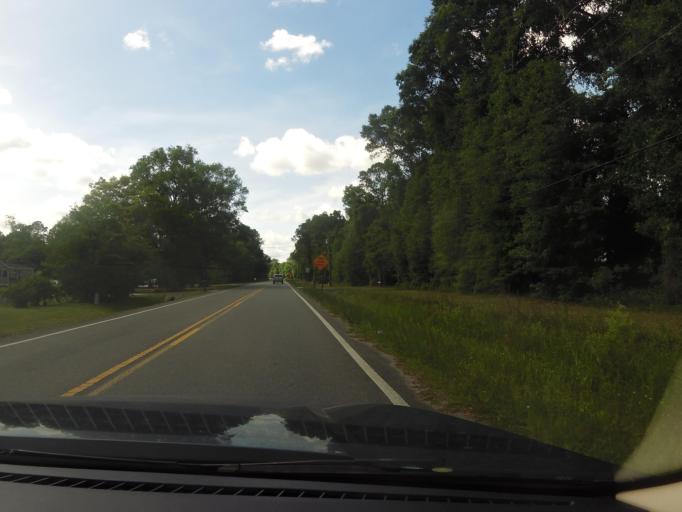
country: US
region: Florida
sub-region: Nassau County
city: Callahan
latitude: 30.5732
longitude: -81.8448
